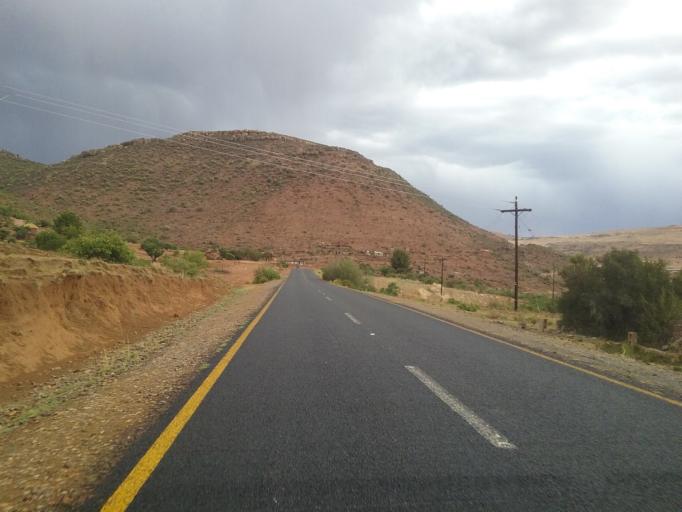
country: LS
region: Quthing
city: Quthing
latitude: -30.3542
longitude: 27.7260
